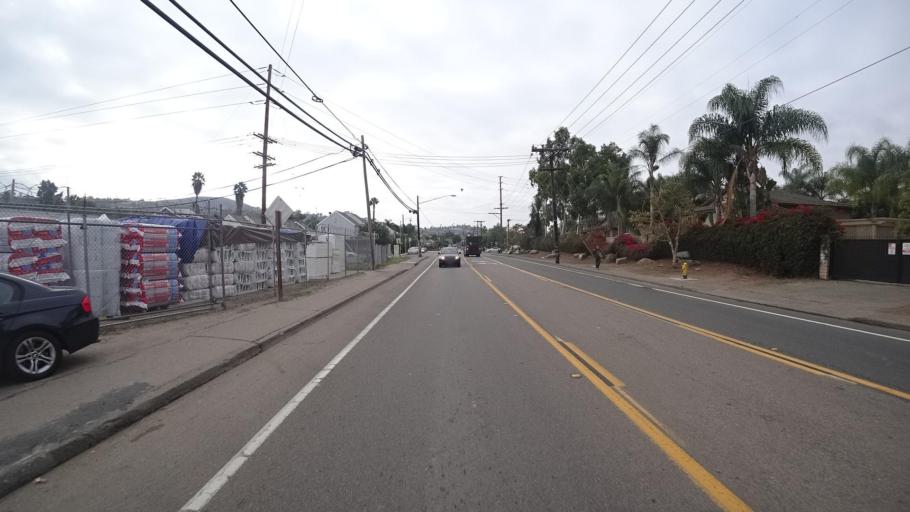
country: US
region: California
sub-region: San Diego County
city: Spring Valley
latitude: 32.7397
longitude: -117.0057
